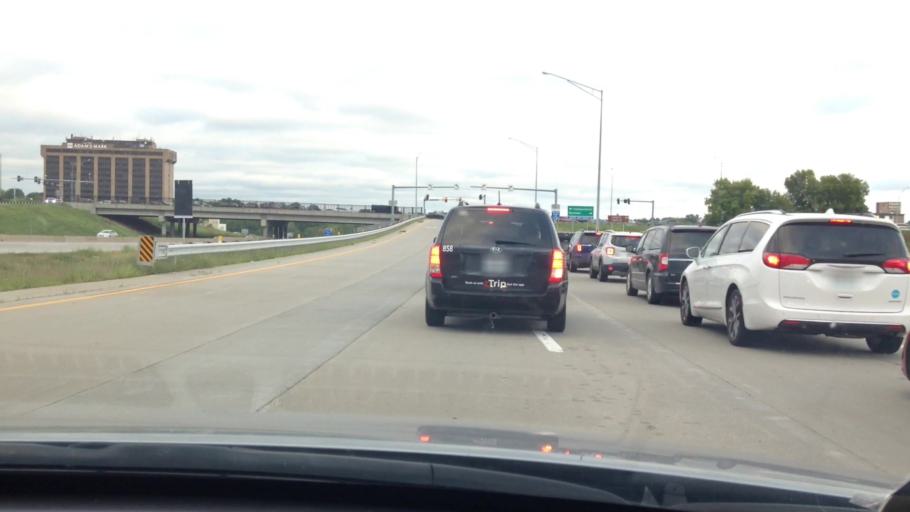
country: US
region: Missouri
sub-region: Jackson County
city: Raytown
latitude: 39.0526
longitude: -94.4770
